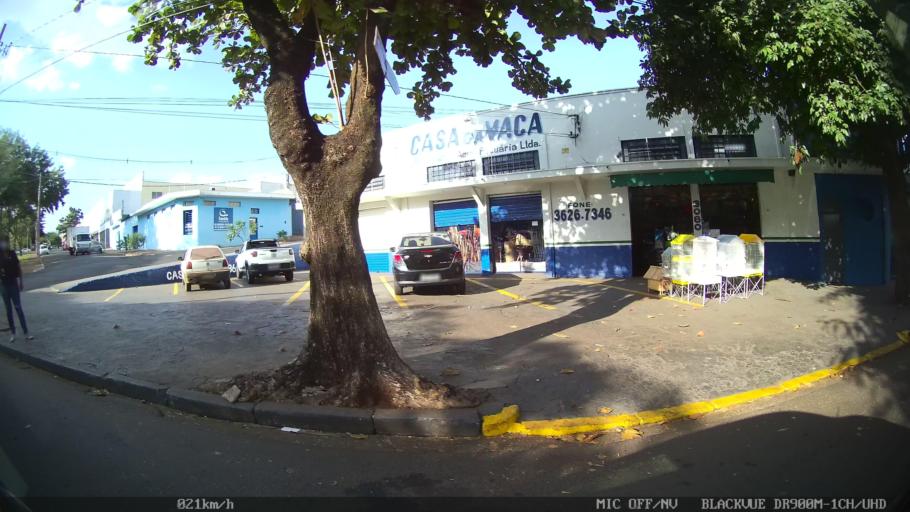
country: BR
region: Sao Paulo
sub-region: Ribeirao Preto
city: Ribeirao Preto
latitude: -21.1440
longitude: -47.7994
